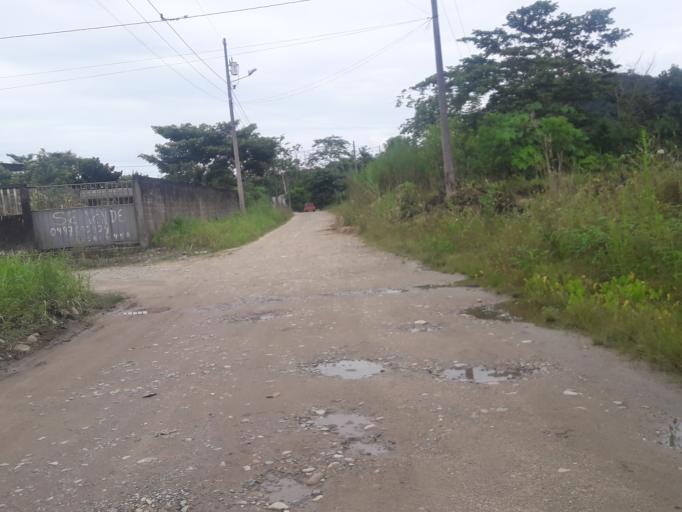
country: EC
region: Napo
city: Tena
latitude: -0.9876
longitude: -77.8321
